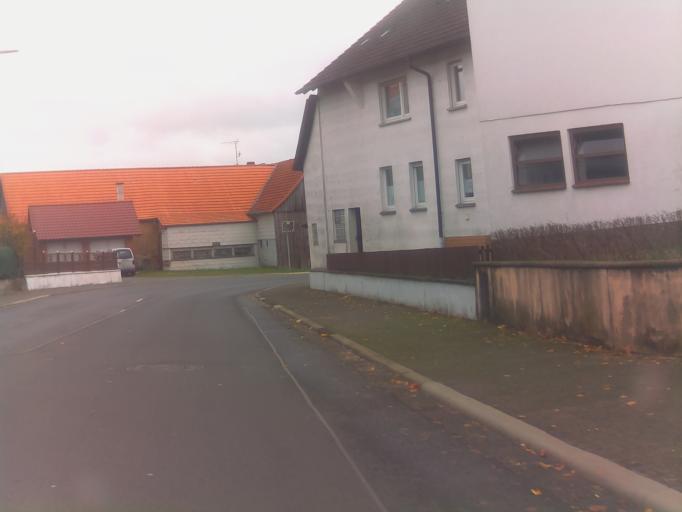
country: DE
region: Hesse
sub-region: Regierungsbezirk Giessen
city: Grebenhain
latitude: 50.5223
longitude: 9.3297
